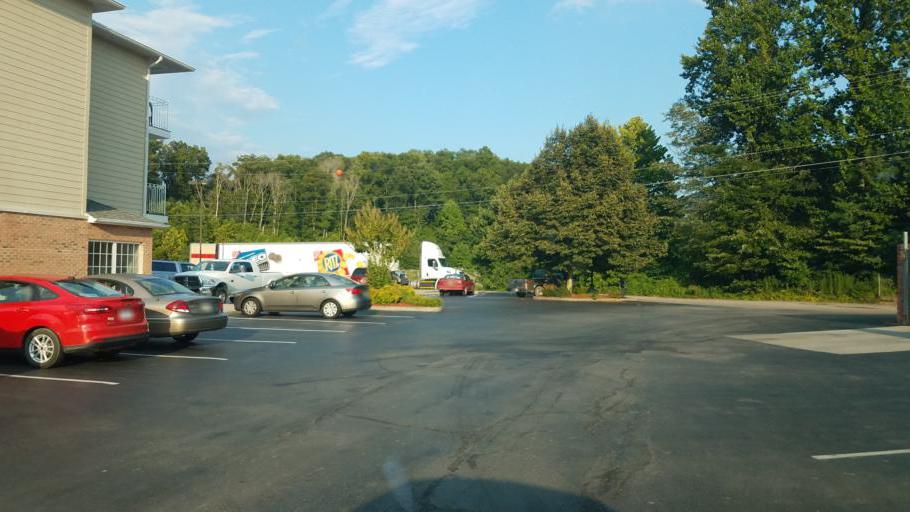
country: US
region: Virginia
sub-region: Wise County
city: Big Stone Gap
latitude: 36.8587
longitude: -82.7528
